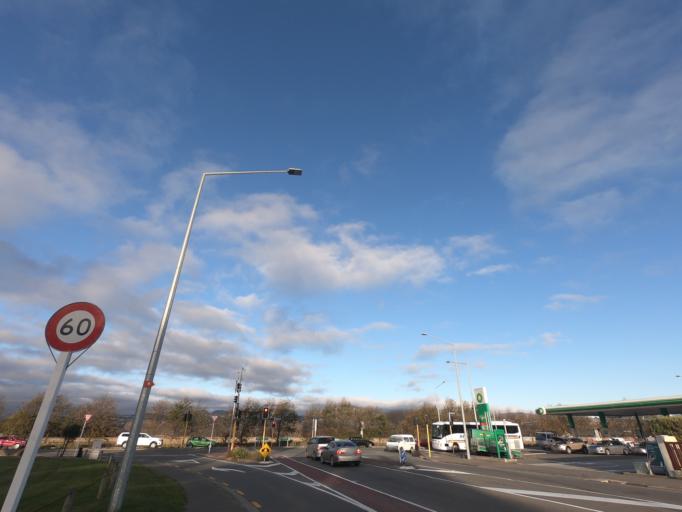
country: NZ
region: Canterbury
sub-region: Selwyn District
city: Prebbleton
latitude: -43.5714
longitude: 172.5707
